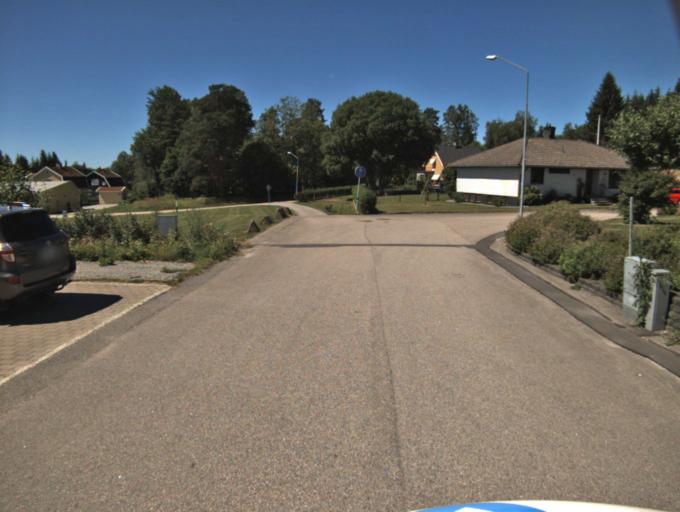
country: SE
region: Vaestra Goetaland
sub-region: Ulricehamns Kommun
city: Ulricehamn
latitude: 57.6672
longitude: 13.4223
